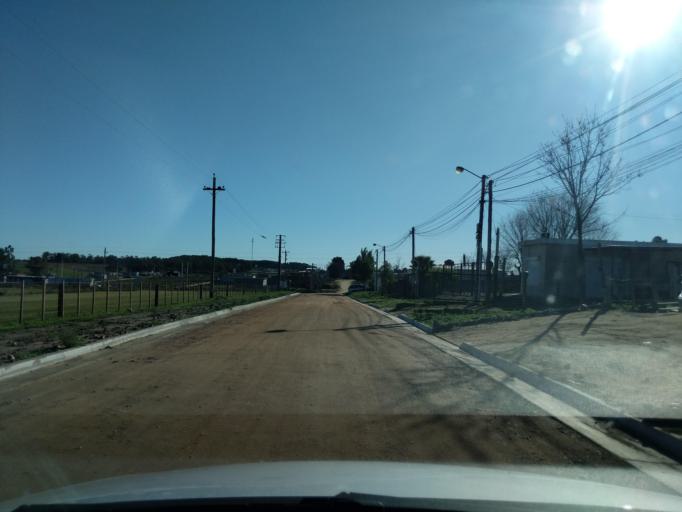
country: UY
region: Florida
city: Florida
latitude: -34.0857
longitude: -56.2403
